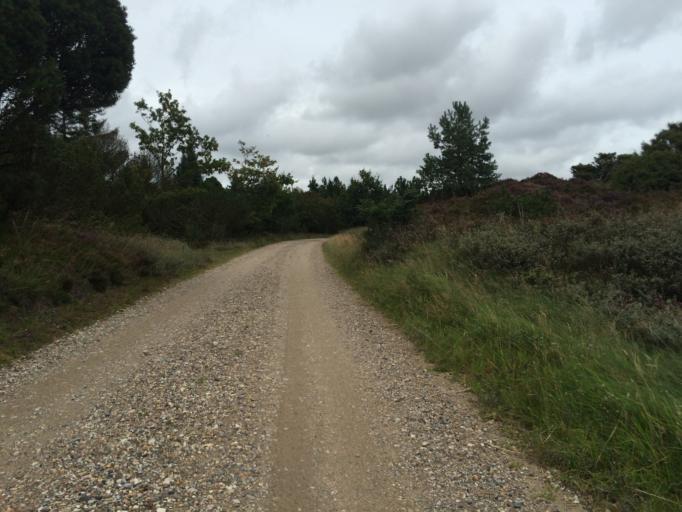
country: DK
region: Central Jutland
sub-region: Holstebro Kommune
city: Ulfborg
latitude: 56.2210
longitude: 8.4013
